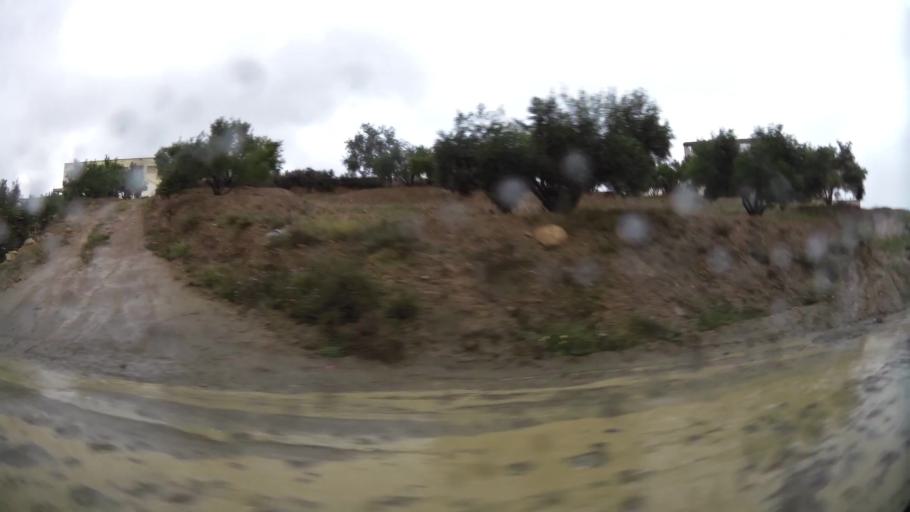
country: MA
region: Oriental
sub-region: Nador
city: Midar
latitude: 34.8900
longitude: -3.7398
